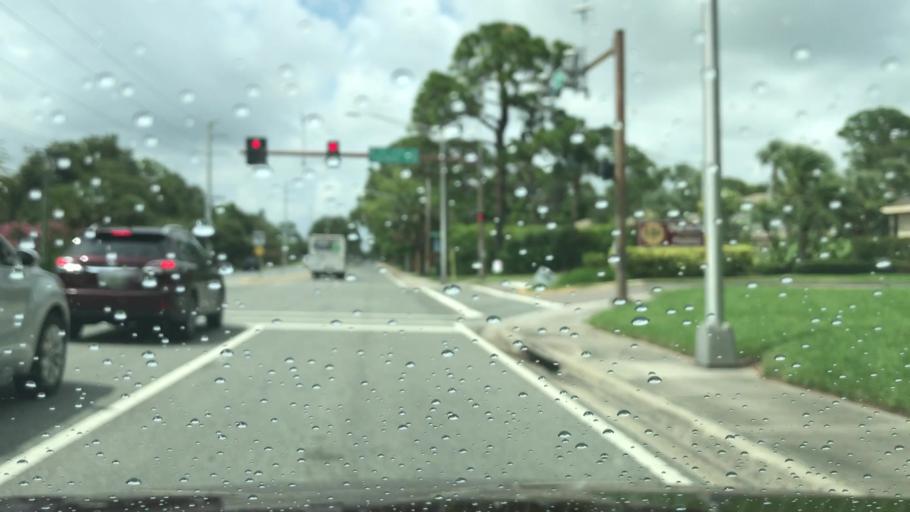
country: US
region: Florida
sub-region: Sarasota County
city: Vamo
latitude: 27.2378
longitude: -82.4975
